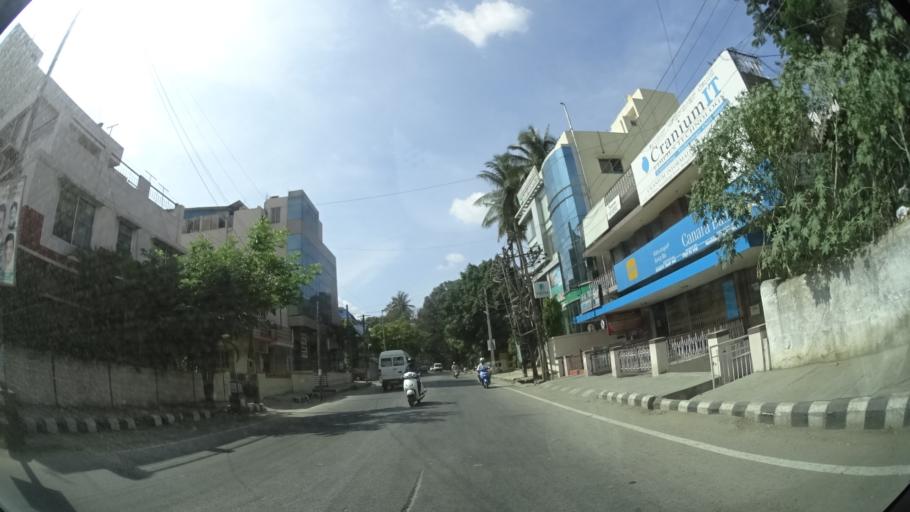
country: IN
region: Karnataka
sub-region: Bangalore Urban
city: Bangalore
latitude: 13.0022
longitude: 77.5983
